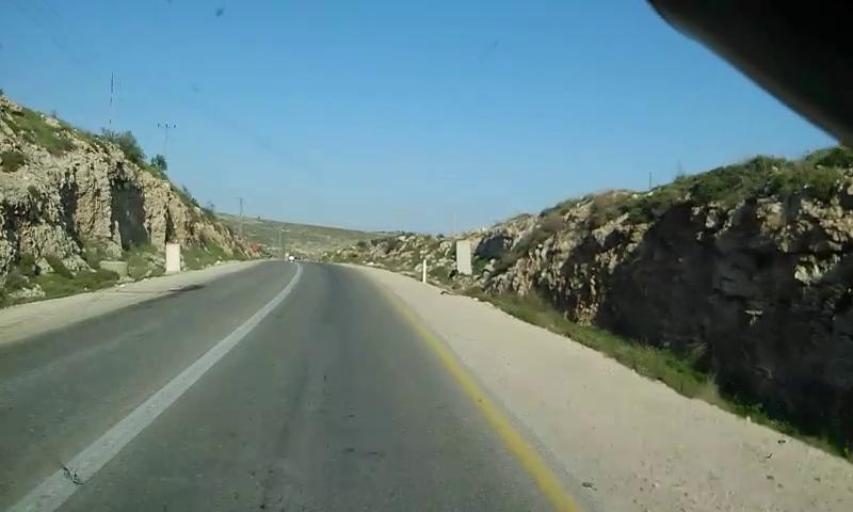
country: PS
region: West Bank
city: Qalqas
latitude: 31.4971
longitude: 35.0946
